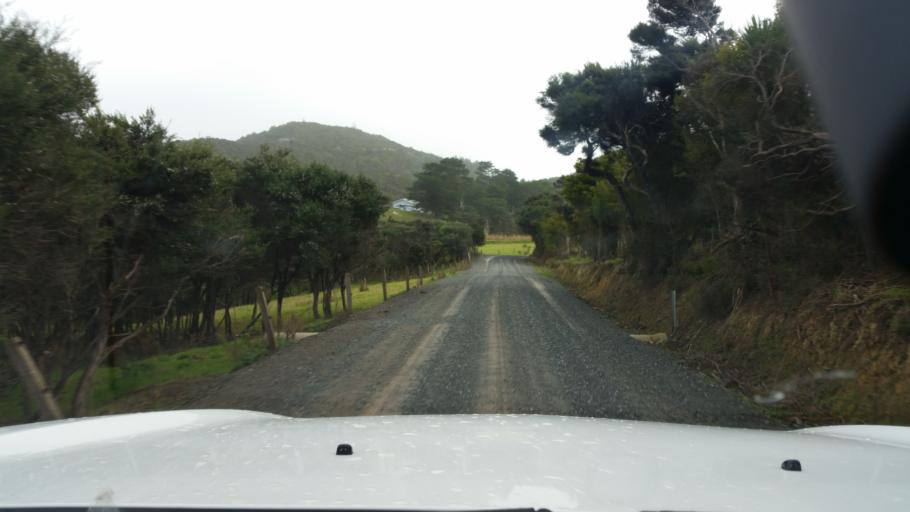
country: NZ
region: Northland
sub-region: Whangarei
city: Ruakaka
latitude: -35.7798
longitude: 174.5456
